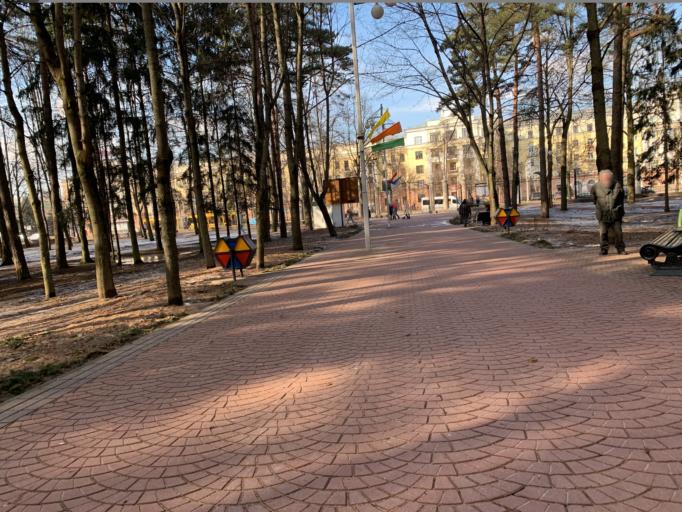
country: BY
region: Minsk
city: Minsk
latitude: 53.9228
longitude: 27.6115
